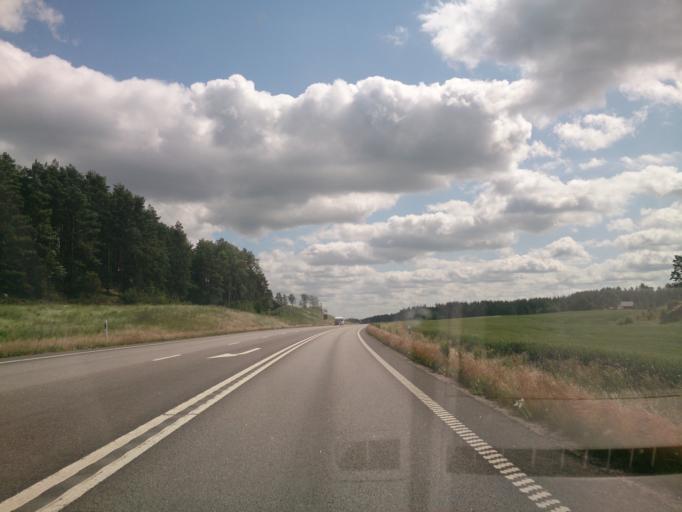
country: SE
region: OEstergoetland
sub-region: Soderkopings Kommun
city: Soederkoeping
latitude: 58.4890
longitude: 16.2499
